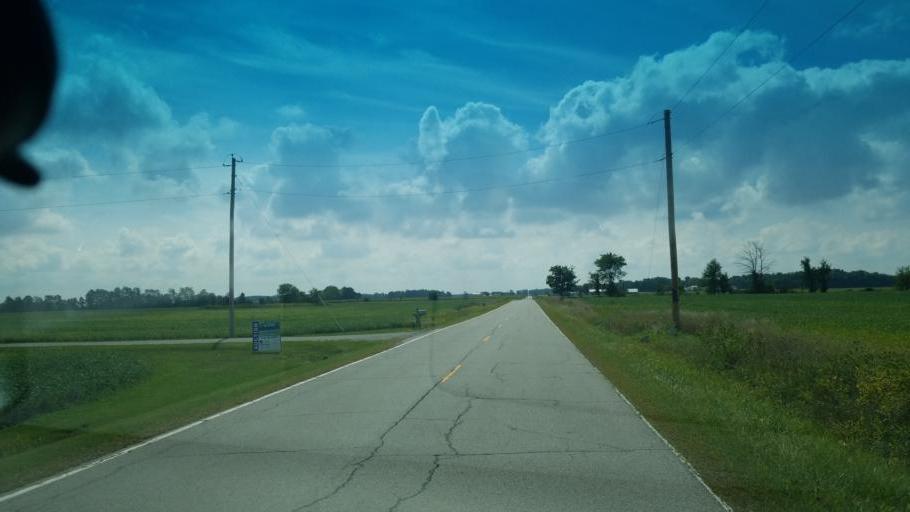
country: US
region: Ohio
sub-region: Crawford County
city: Bucyrus
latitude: 40.9314
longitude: -82.9017
